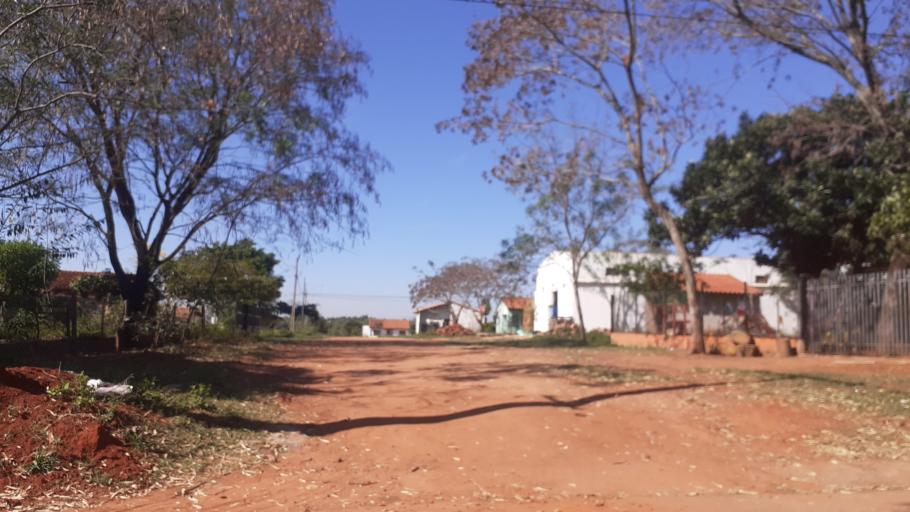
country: PY
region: Misiones
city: San Juan Bautista
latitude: -26.6642
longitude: -57.1253
